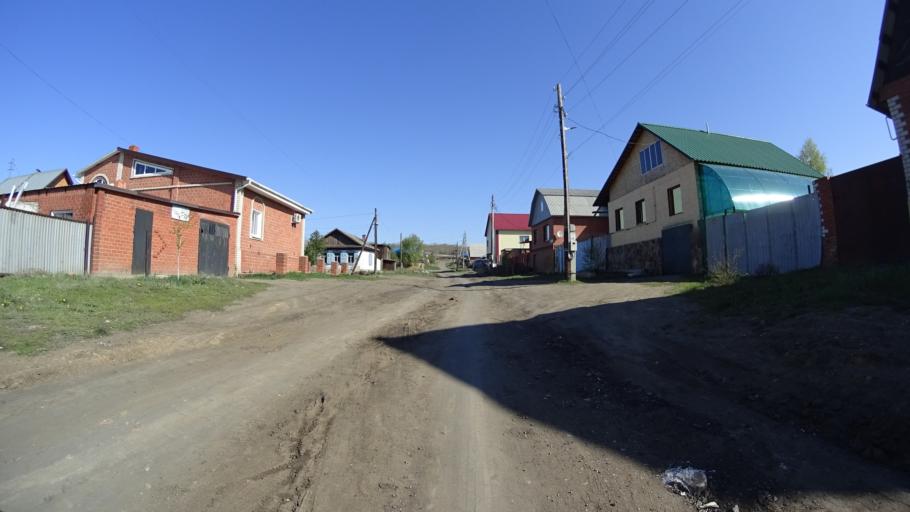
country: RU
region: Chelyabinsk
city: Troitsk
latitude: 54.0973
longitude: 61.5968
